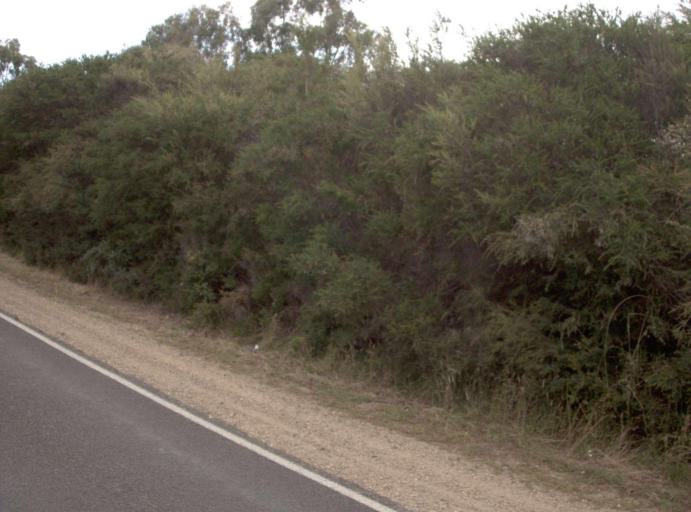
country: AU
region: Victoria
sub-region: Wellington
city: Sale
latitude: -38.1856
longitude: 147.0918
